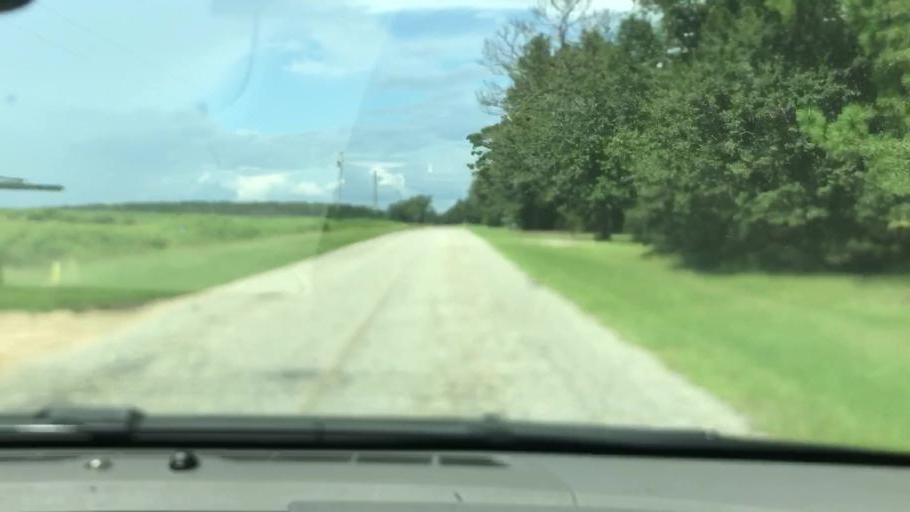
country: US
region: Georgia
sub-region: Early County
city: Blakely
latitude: 31.2097
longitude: -85.0034
